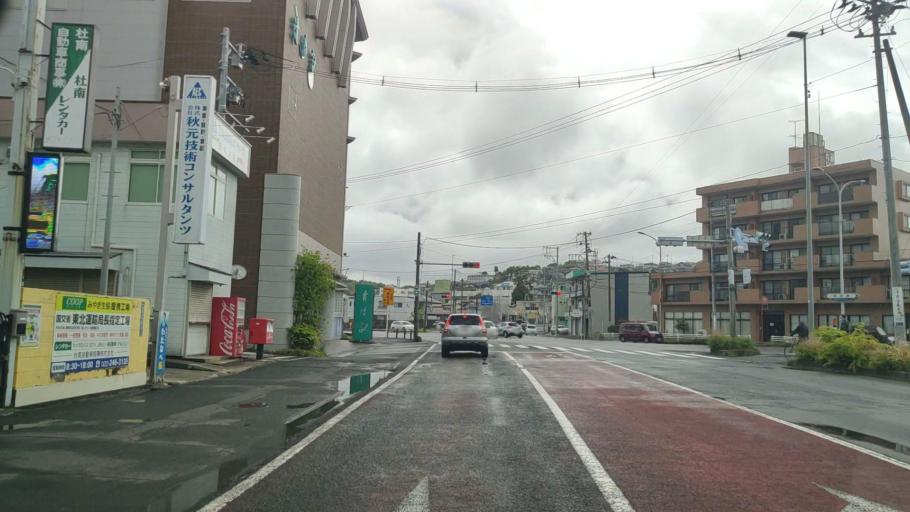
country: JP
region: Miyagi
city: Sendai
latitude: 38.2275
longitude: 140.8719
